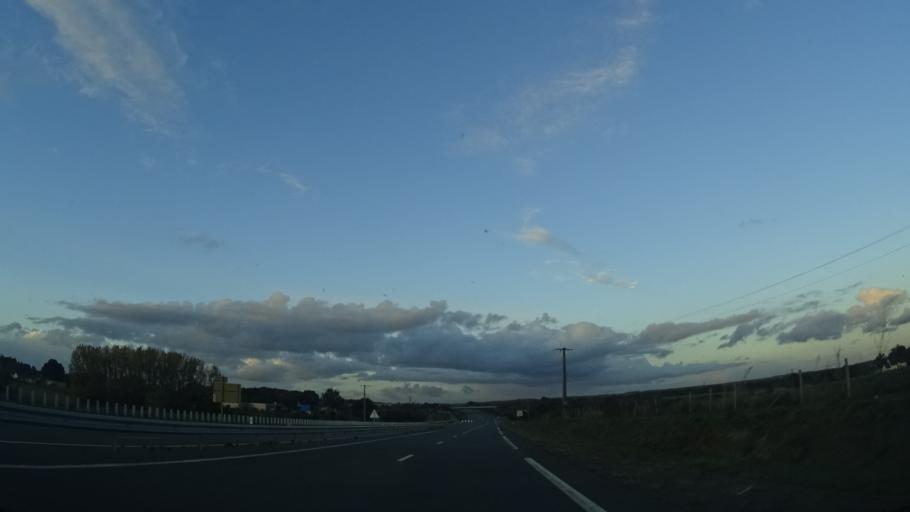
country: FR
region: Brittany
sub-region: Departement d'Ille-et-Vilaine
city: Pipriac
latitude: 47.8306
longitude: -1.9089
